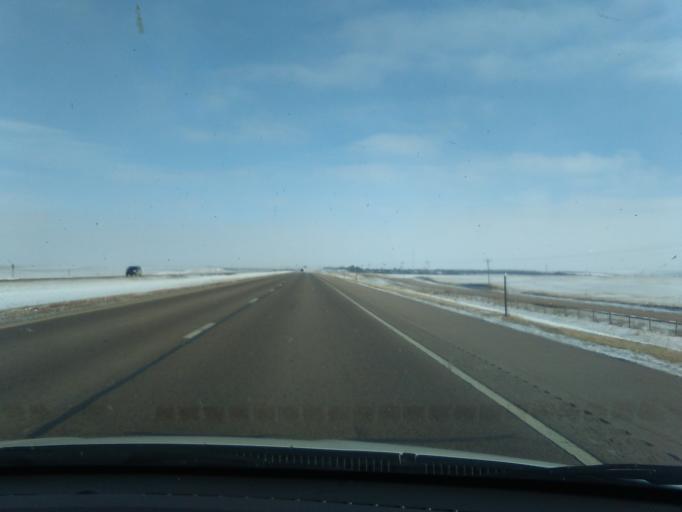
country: US
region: Nebraska
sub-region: Kimball County
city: Kimball
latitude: 41.1918
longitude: -103.7880
